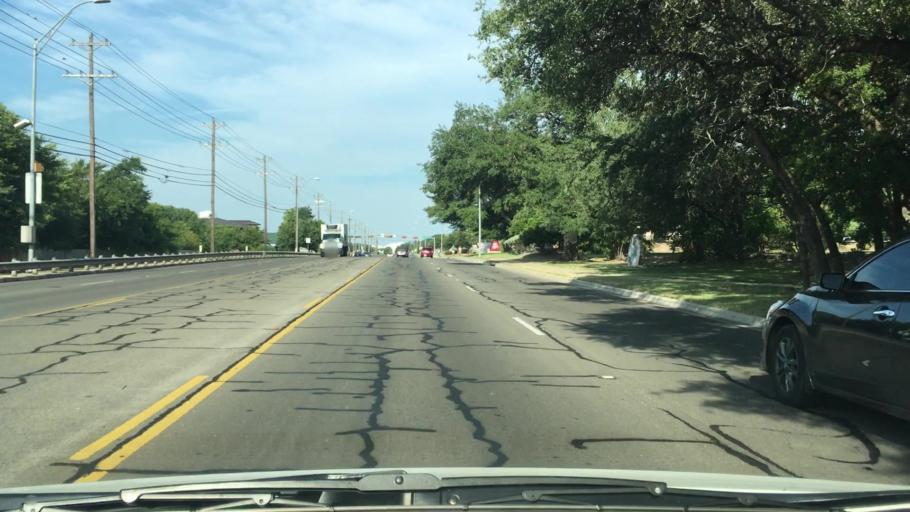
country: US
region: Texas
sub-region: Williamson County
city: Cedar Park
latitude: 30.4759
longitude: -97.8388
